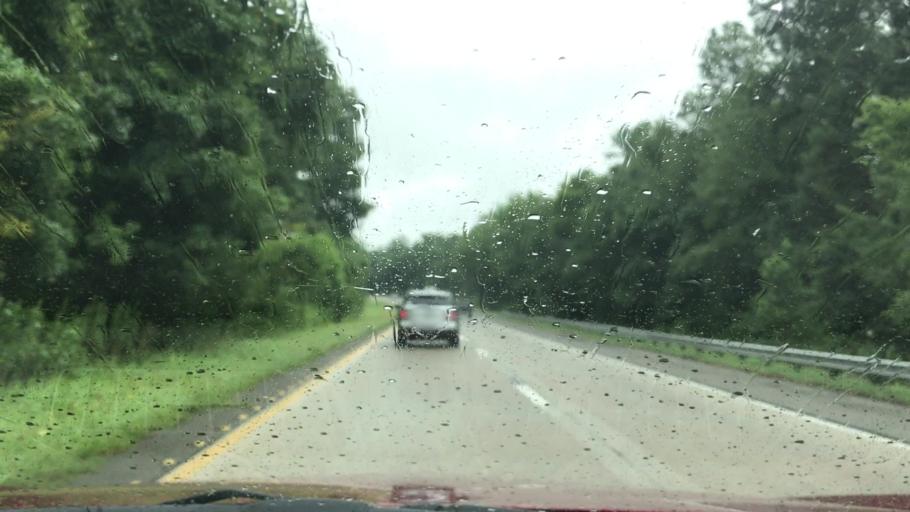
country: US
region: South Carolina
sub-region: Orangeburg County
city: Holly Hill
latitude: 33.2397
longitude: -80.4598
